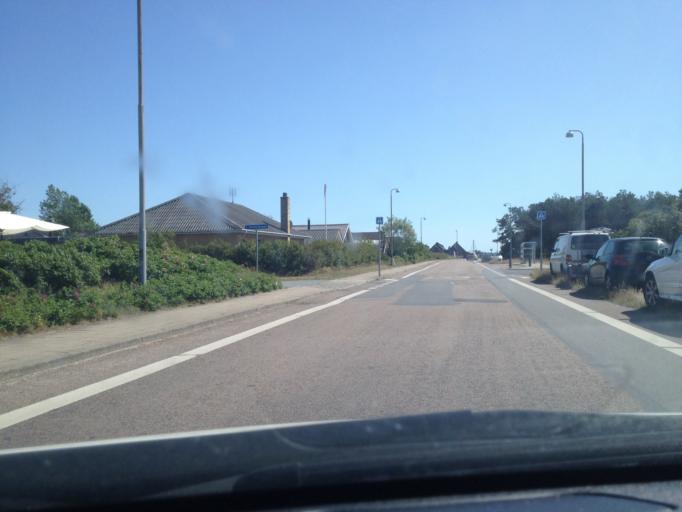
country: DE
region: Schleswig-Holstein
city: List
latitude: 55.0891
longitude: 8.5514
